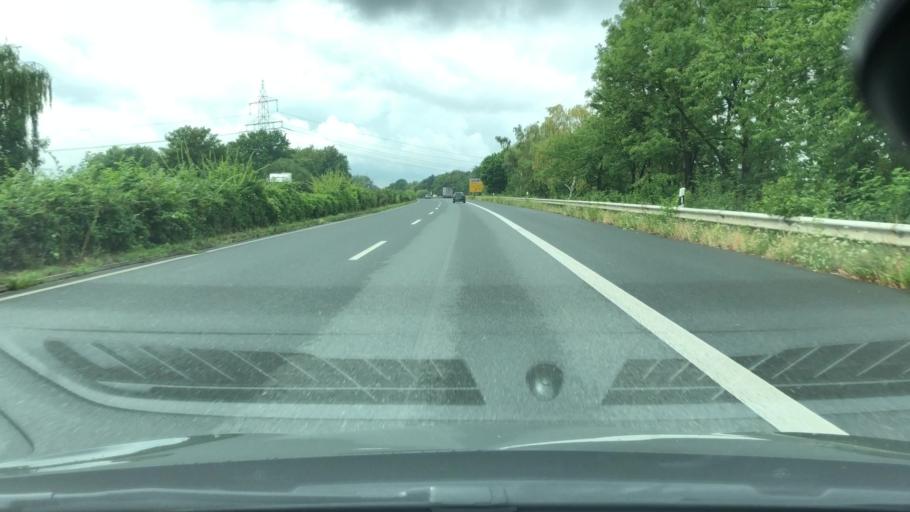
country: DE
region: North Rhine-Westphalia
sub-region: Regierungsbezirk Detmold
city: Minden
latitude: 52.2697
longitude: 8.9681
